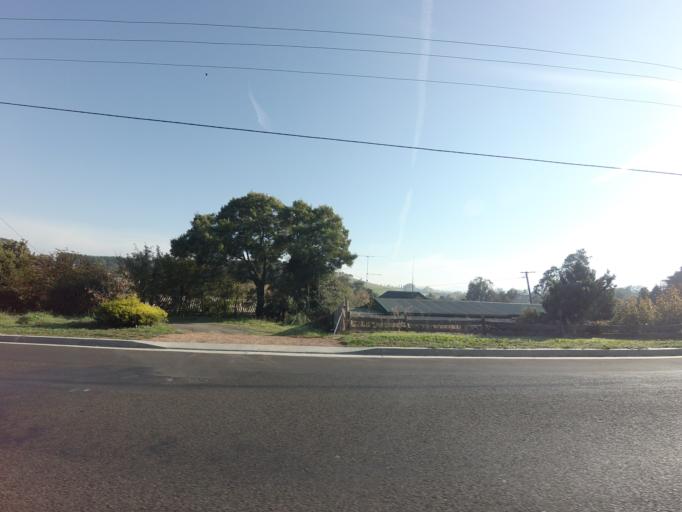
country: AU
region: Tasmania
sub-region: Northern Midlands
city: Longford
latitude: -41.5330
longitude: 147.0059
